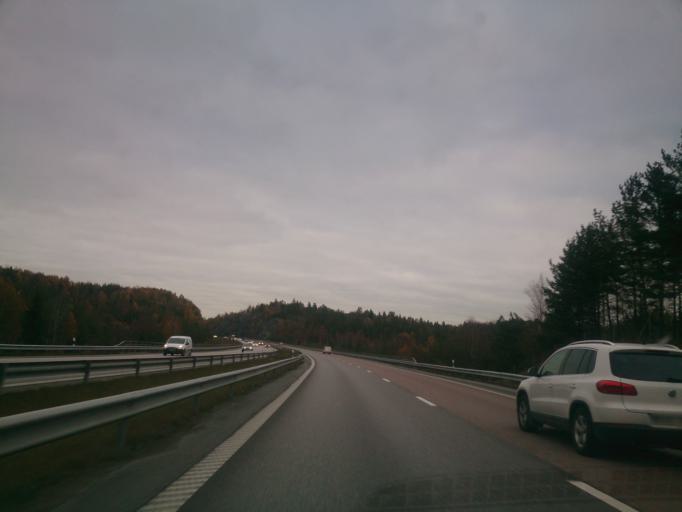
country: SE
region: Stockholm
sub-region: Sodertalje Kommun
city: Pershagen
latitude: 59.1285
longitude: 17.6387
